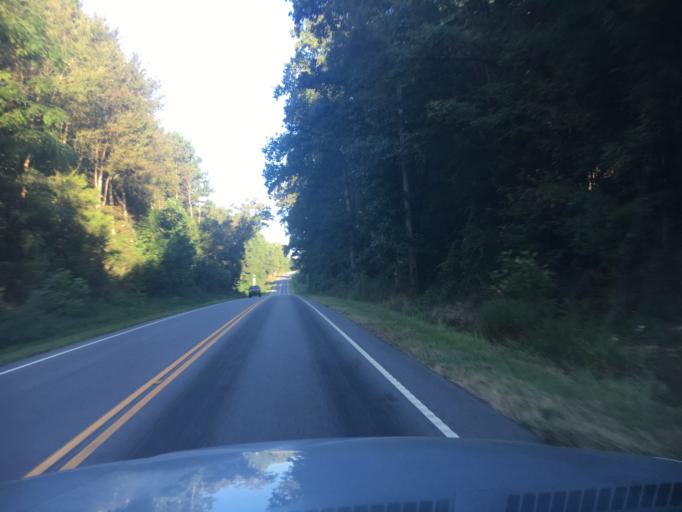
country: US
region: South Carolina
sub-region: Spartanburg County
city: Woodruff
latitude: 34.6996
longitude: -81.9466
